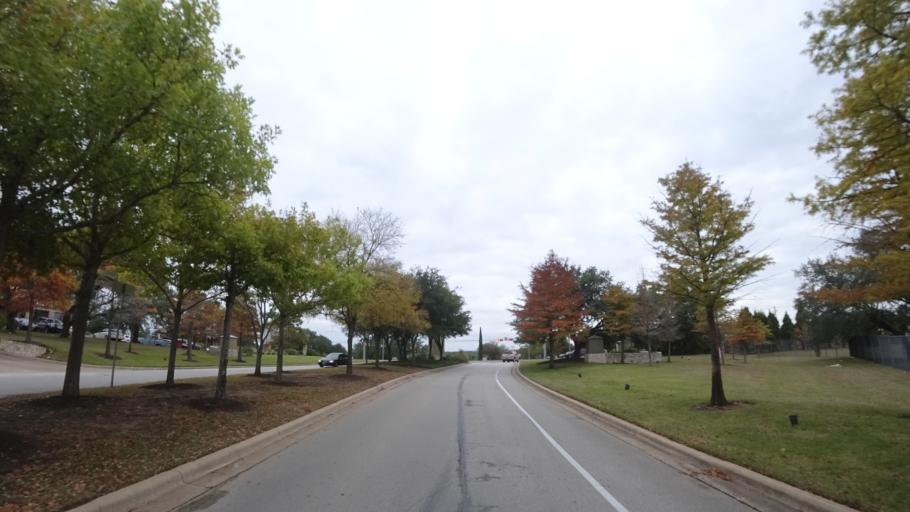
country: US
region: Texas
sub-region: Travis County
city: Bee Cave
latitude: 30.3100
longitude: -97.9186
